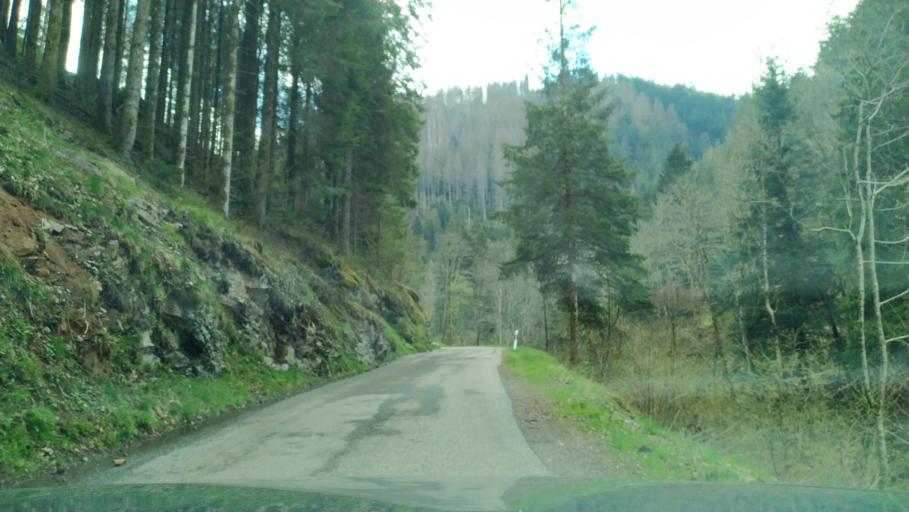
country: DE
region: Baden-Wuerttemberg
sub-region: Freiburg Region
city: Sankt Margen
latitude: 48.0179
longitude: 8.1260
